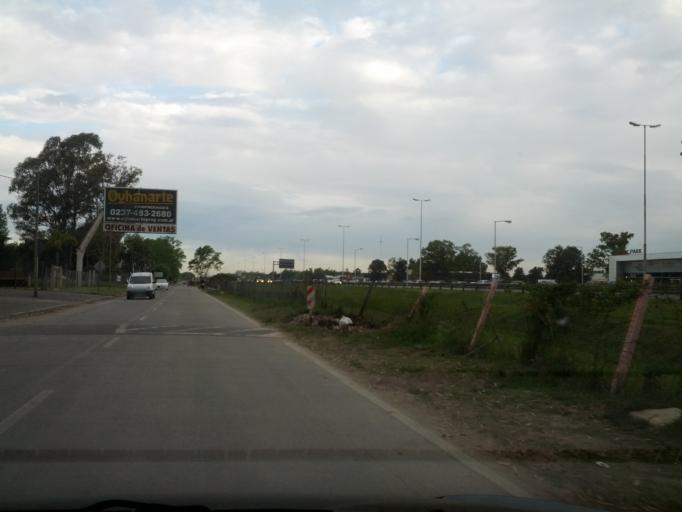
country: AR
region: Buenos Aires
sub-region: Partido de General Rodriguez
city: General Rodriguez
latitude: -34.6103
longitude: -58.8678
